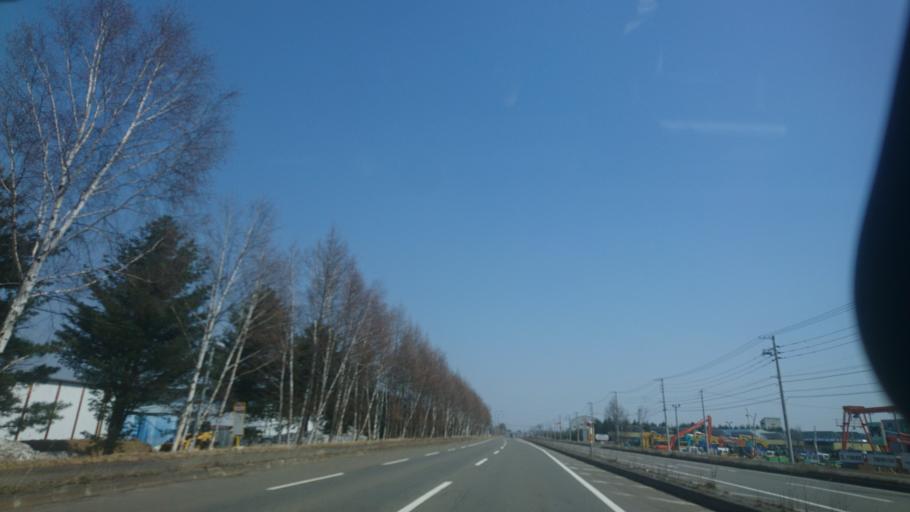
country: JP
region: Hokkaido
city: Obihiro
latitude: 42.9239
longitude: 143.0900
